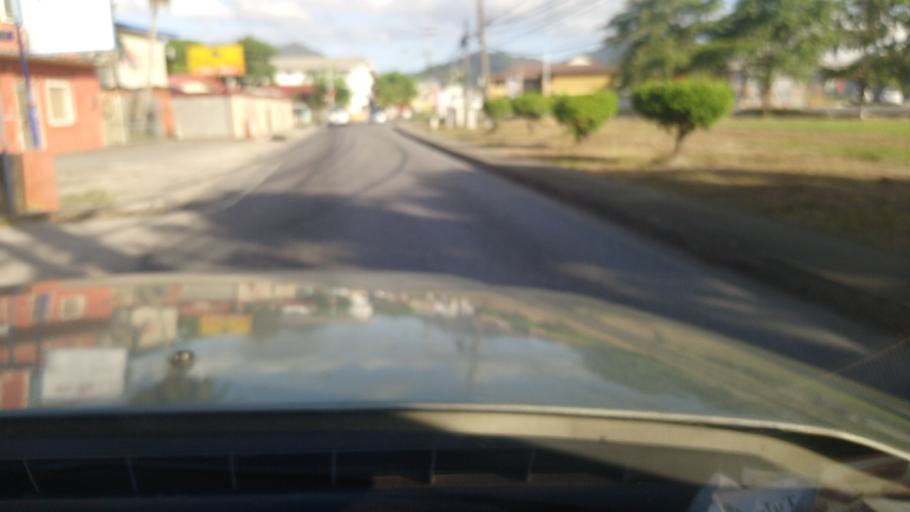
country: TT
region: Borough of Arima
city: Arima
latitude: 10.6298
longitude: -61.2754
